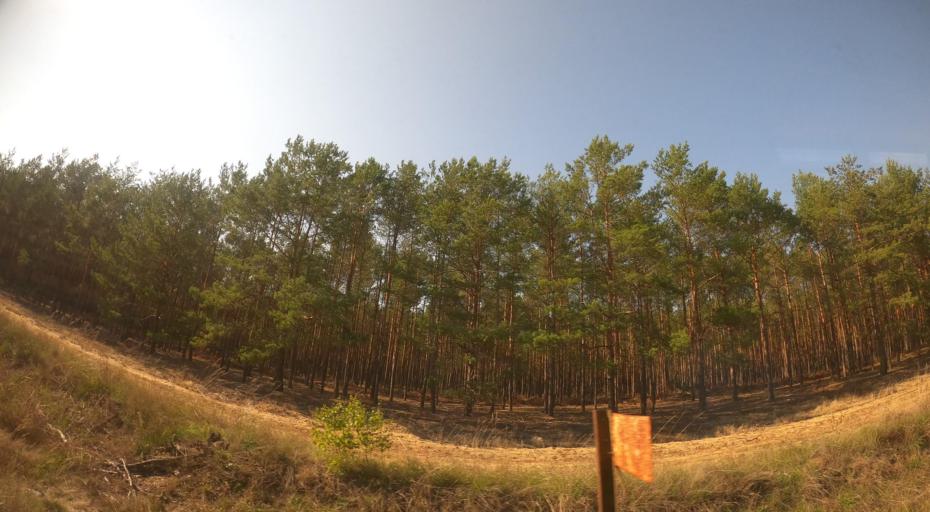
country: PL
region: Lubusz
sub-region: Powiat zielonogorski
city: Nowogrod Bobrzanski
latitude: 51.8182
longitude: 15.2489
